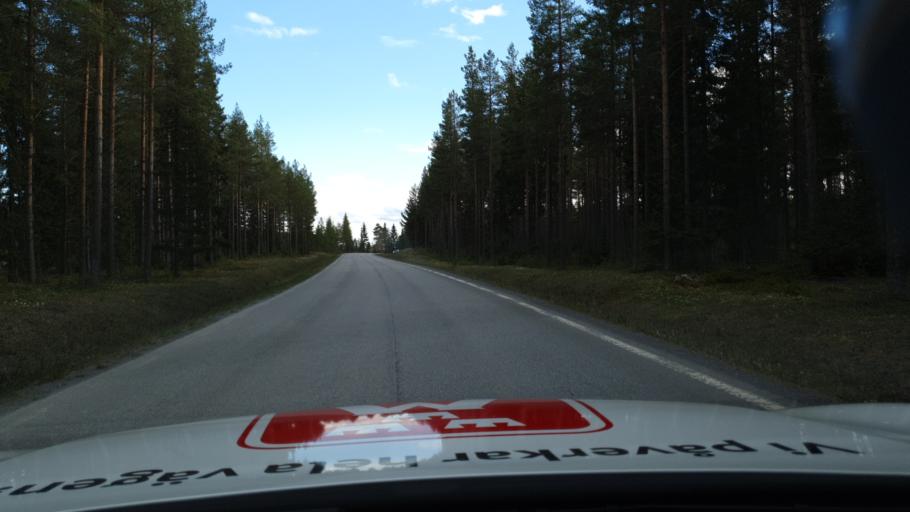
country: SE
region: Jaemtland
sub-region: Krokoms Kommun
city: Krokom
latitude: 63.2535
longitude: 14.4275
